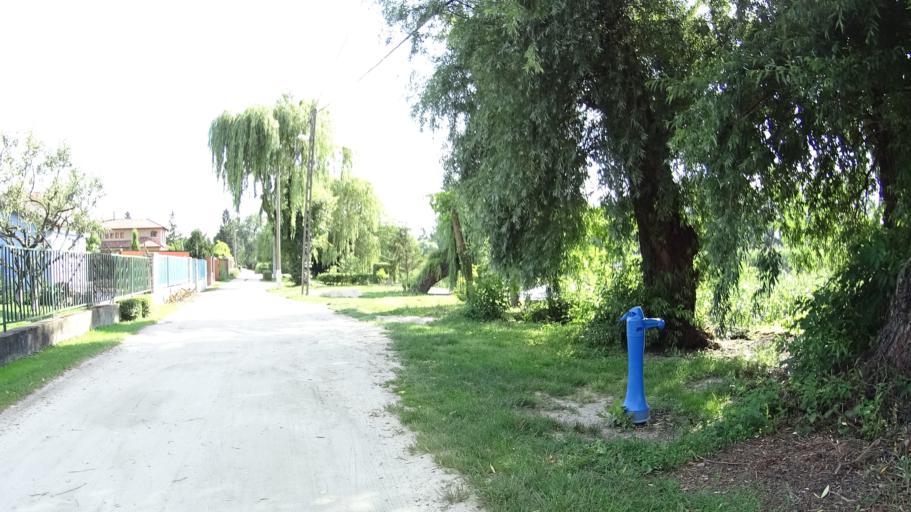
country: HU
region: Budapest
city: Budapest XXIII. keruelet
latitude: 47.3791
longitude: 19.0993
